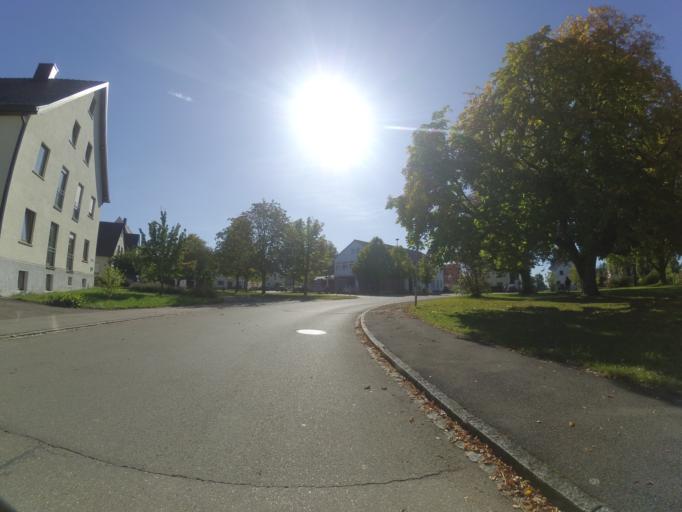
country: DE
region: Baden-Wuerttemberg
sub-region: Tuebingen Region
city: Neenstetten
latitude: 48.5458
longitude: 10.0203
